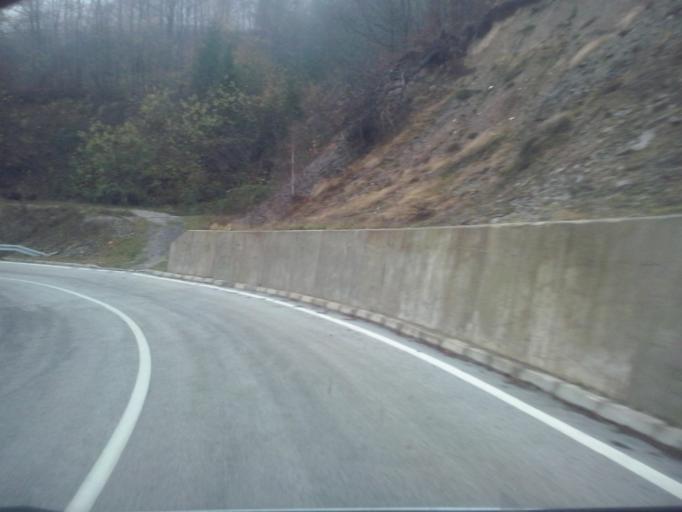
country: RS
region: Central Serbia
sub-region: Moravicki Okrug
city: Ivanjica
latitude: 43.5369
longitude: 20.2980
